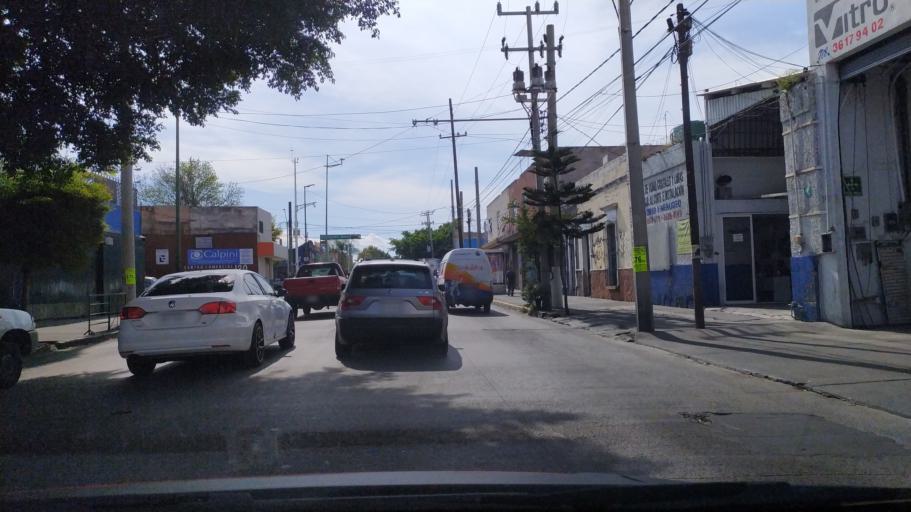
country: MX
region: Jalisco
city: Tlaquepaque
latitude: 20.6731
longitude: -103.3303
